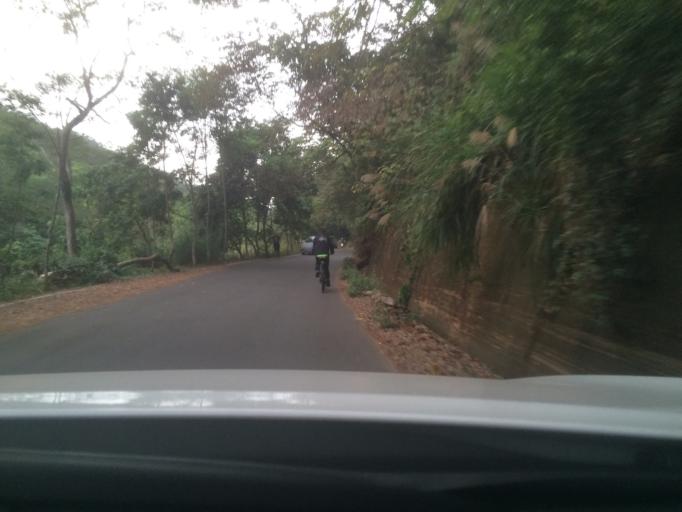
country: TW
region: Taiwan
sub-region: Nantou
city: Nantou
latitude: 23.9318
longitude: 120.6342
